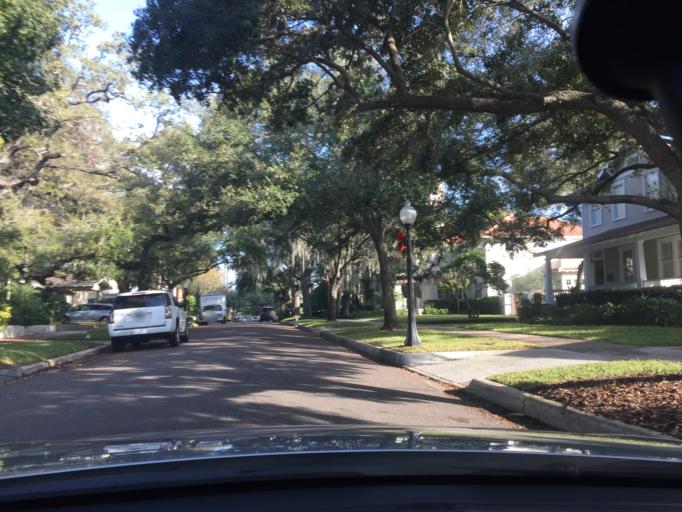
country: US
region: Florida
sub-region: Hillsborough County
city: Tampa
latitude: 27.9324
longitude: -82.4758
